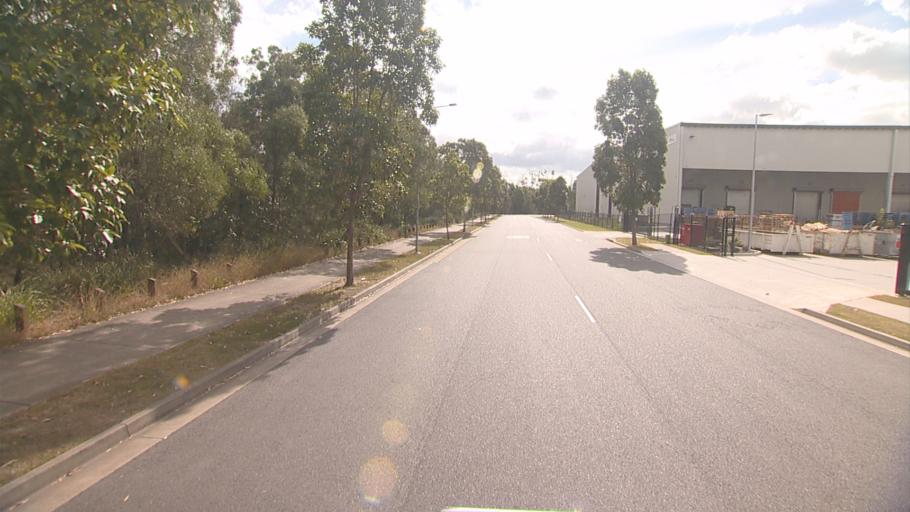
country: AU
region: Queensland
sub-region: Logan
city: Woodridge
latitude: -27.6678
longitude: 153.0759
